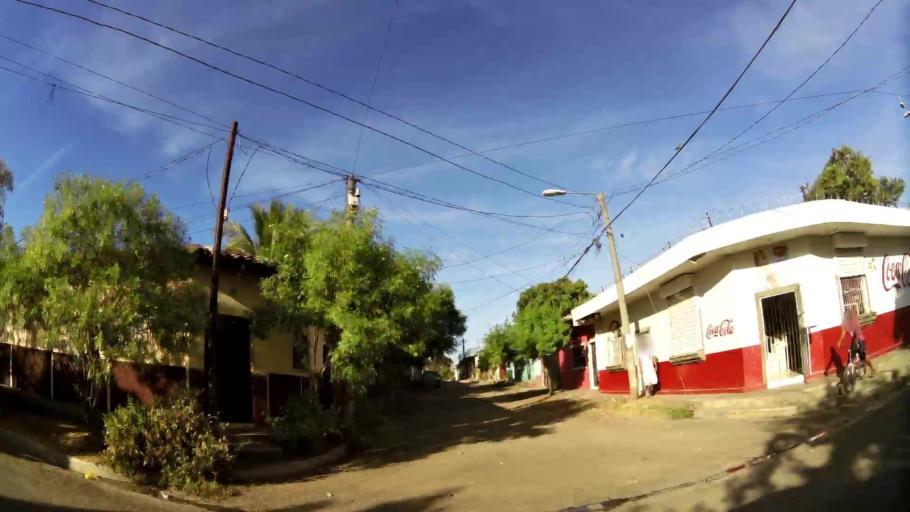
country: SV
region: San Miguel
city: San Miguel
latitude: 13.4631
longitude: -88.1756
